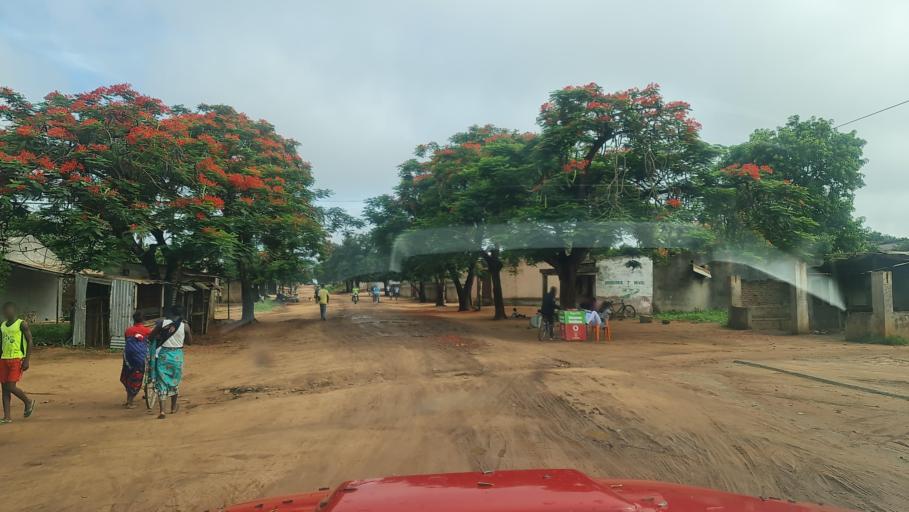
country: MW
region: Southern Region
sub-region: Nsanje District
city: Nsanje
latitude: -17.3255
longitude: 35.5915
